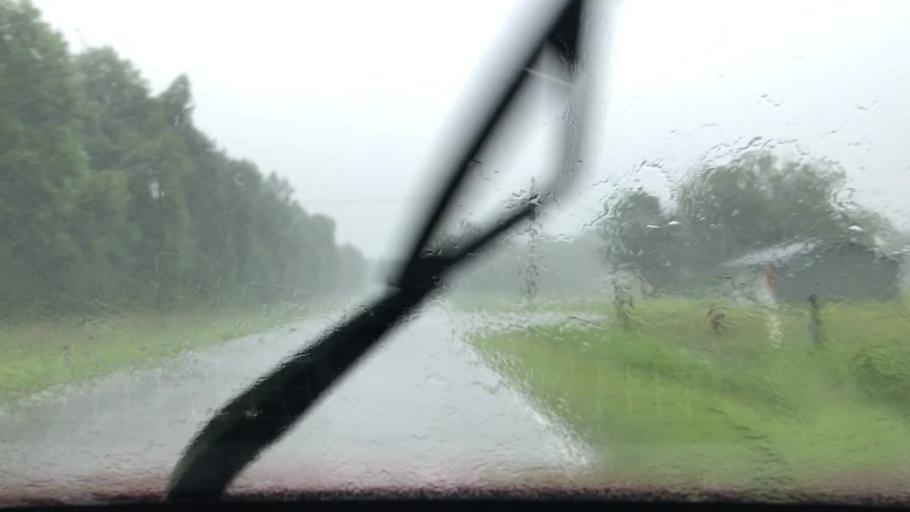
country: US
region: South Carolina
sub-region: Horry County
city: Red Hill
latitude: 33.9021
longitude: -78.9179
